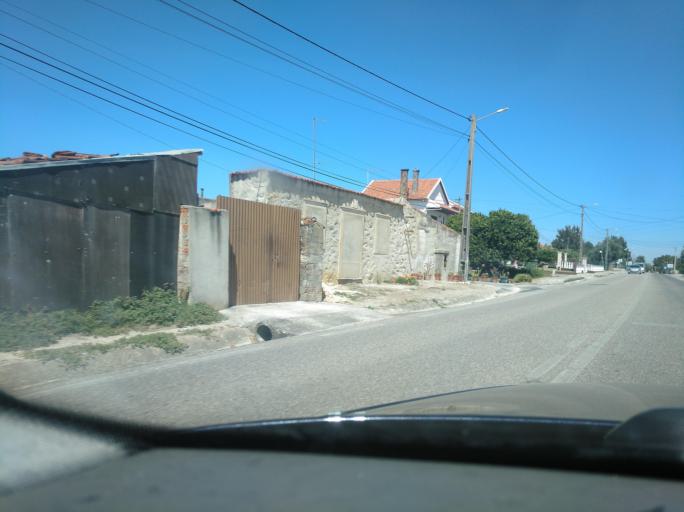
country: PT
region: Leiria
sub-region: Alcobaca
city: Aljubarrota
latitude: 39.5716
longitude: -8.9186
